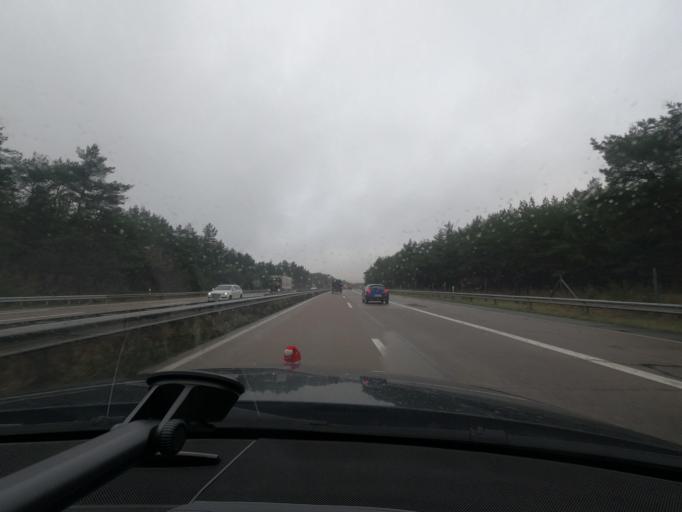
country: DE
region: Lower Saxony
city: Soltau
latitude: 53.0055
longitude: 9.9289
